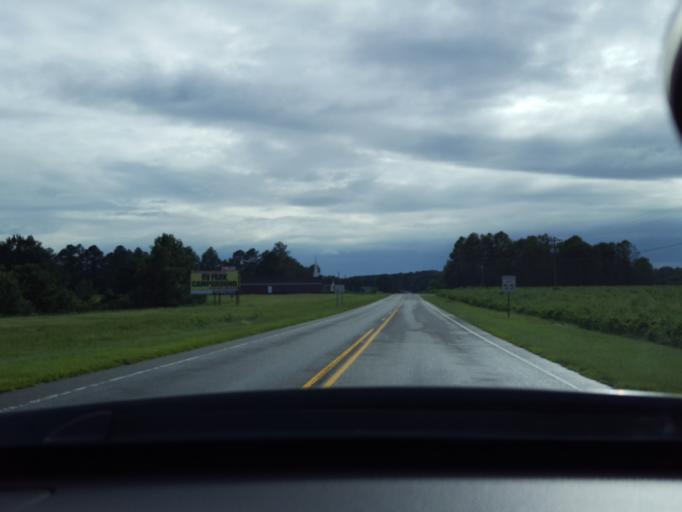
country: US
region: North Carolina
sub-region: Duplin County
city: Kenansville
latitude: 34.9163
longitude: -78.0268
